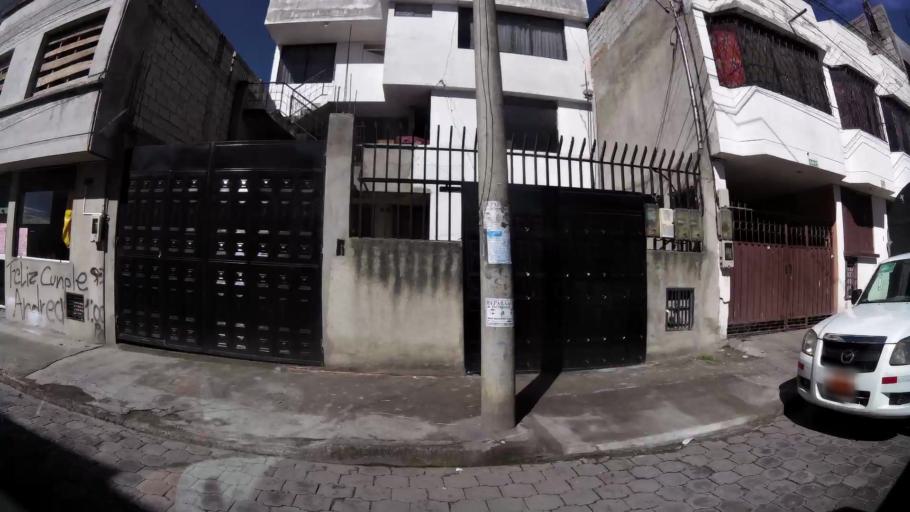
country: EC
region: Pichincha
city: Quito
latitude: -0.2981
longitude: -78.5682
